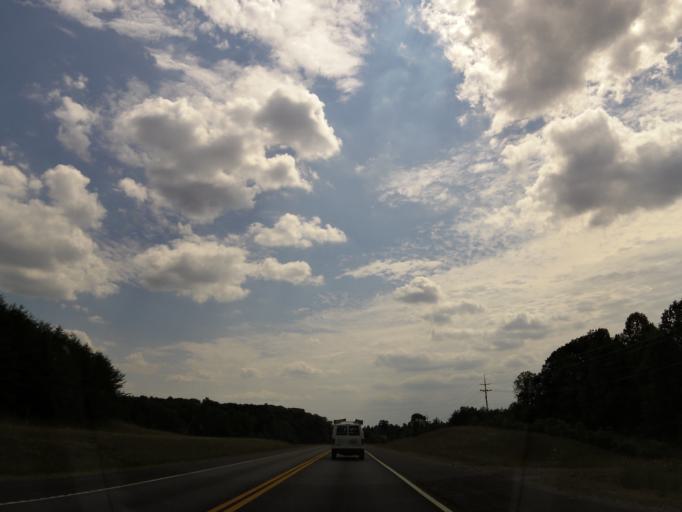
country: US
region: Tennessee
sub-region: Marion County
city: Whitwell
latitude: 35.1339
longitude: -85.5521
